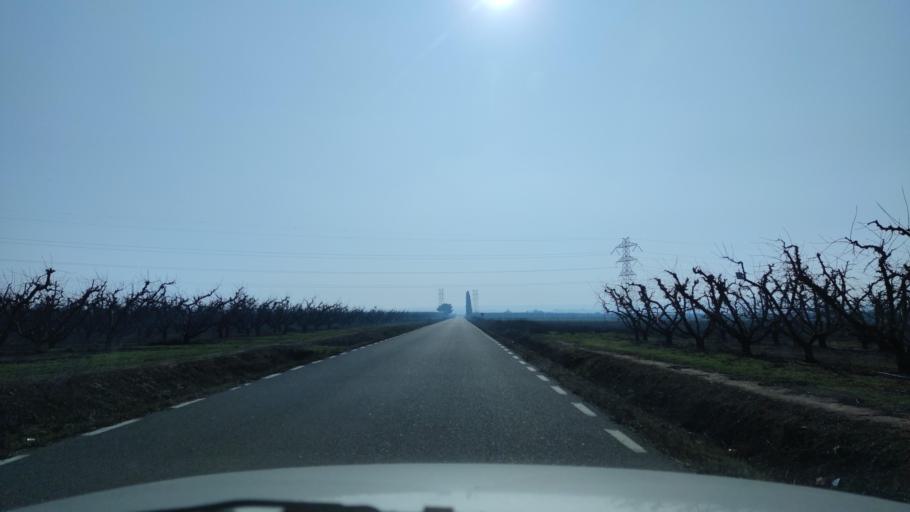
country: ES
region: Catalonia
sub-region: Provincia de Lleida
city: Sunyer
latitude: 41.5517
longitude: 0.5738
